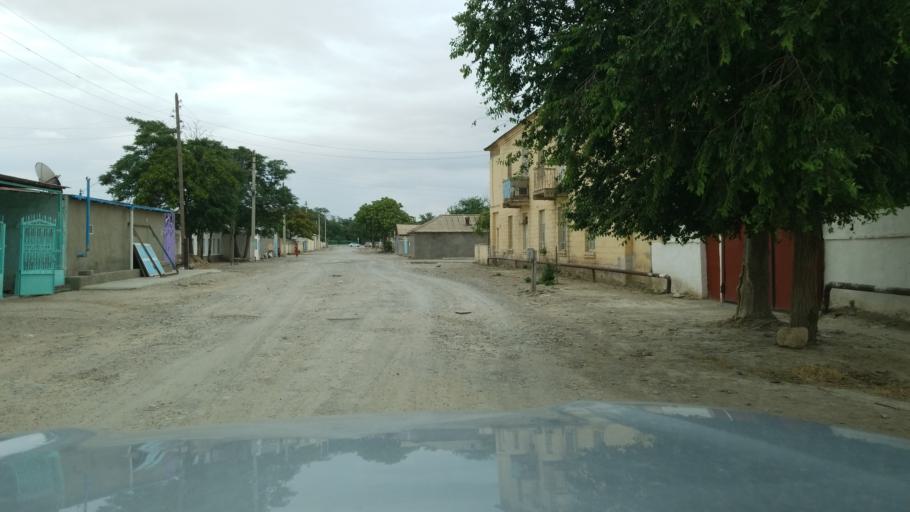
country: TM
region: Balkan
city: Serdar
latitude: 38.9804
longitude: 56.2720
